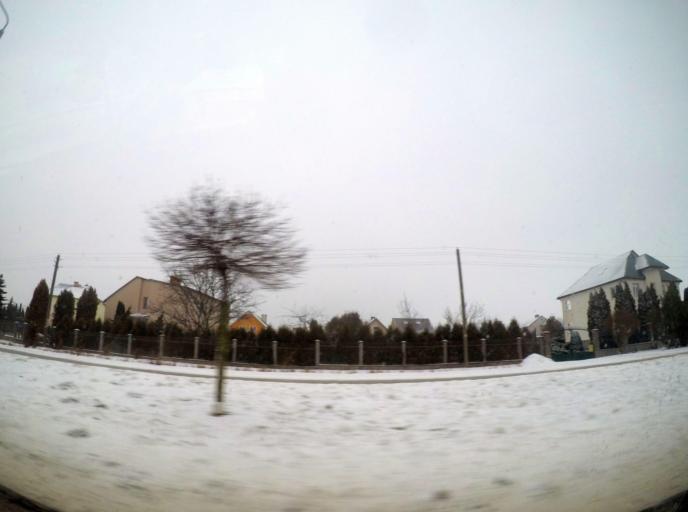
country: BY
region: Grodnenskaya
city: Hrodna
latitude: 53.6265
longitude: 23.8052
